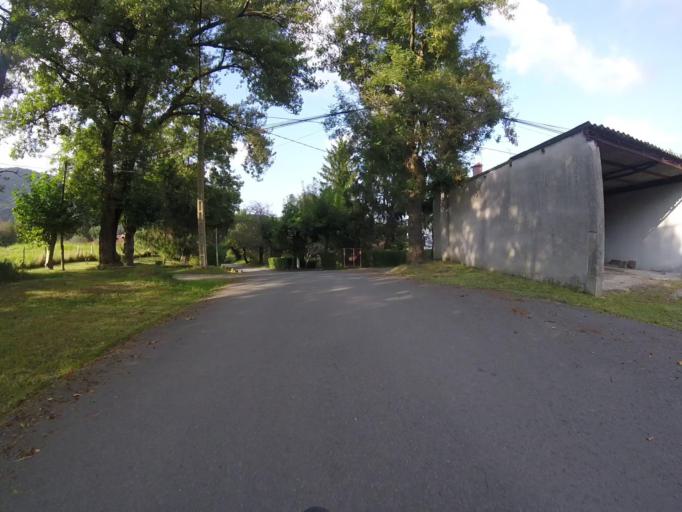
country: ES
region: Basque Country
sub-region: Provincia de Guipuzcoa
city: Fuenterrabia
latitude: 43.3495
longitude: -1.8195
